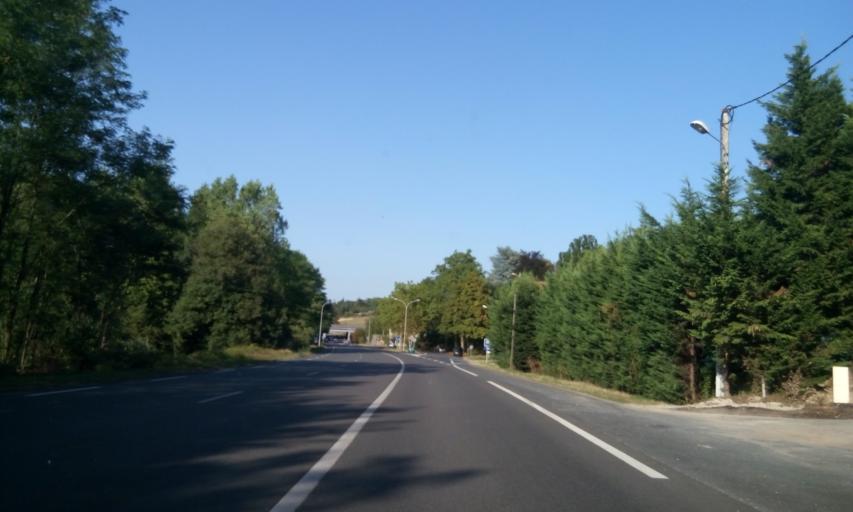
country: FR
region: Rhone-Alpes
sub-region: Departement du Rhone
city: Lissieu
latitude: 45.8563
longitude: 4.7375
